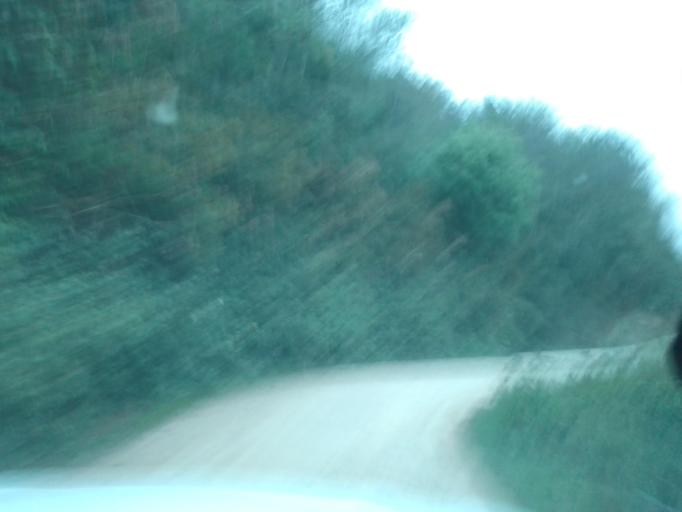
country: MX
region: Chiapas
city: Motozintla de Mendoza
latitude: 15.2238
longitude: -92.2381
